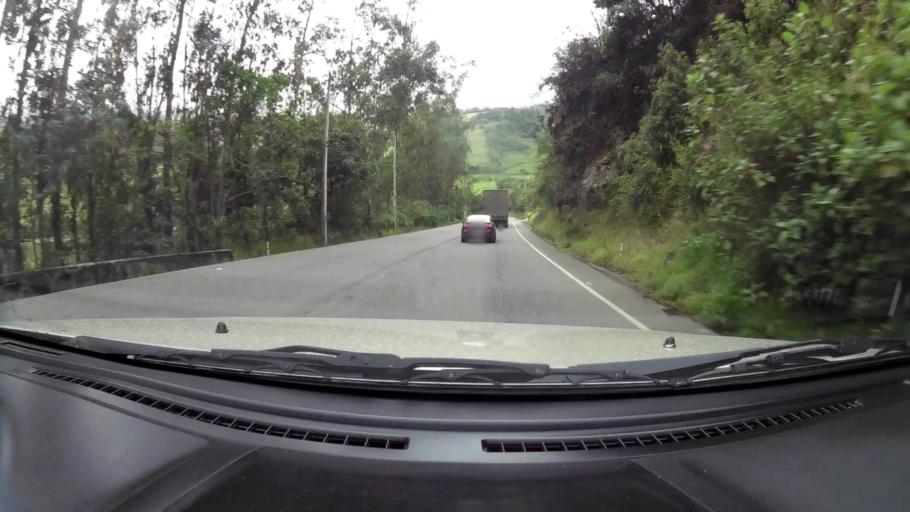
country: EC
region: Canar
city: Canar
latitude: -2.3832
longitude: -78.9670
